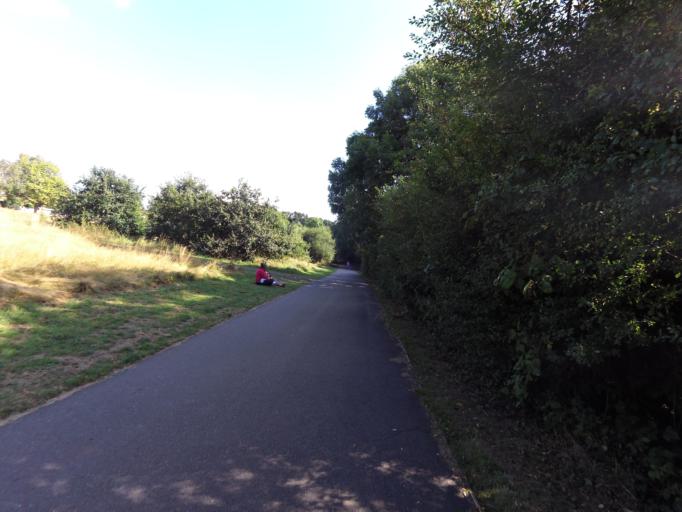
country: GB
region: England
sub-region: Greater London
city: Wood Green
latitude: 51.6294
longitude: -0.1437
